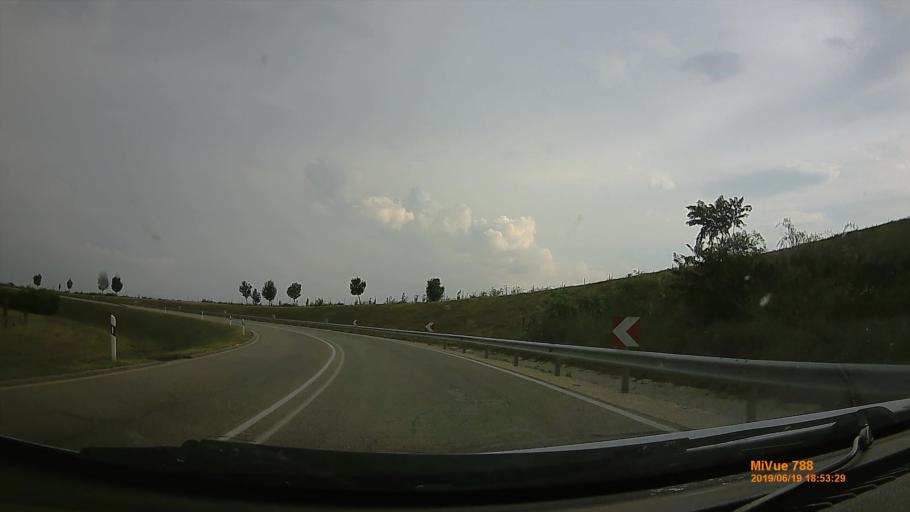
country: HU
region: Fejer
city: Rackeresztur
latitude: 47.3076
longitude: 18.8653
